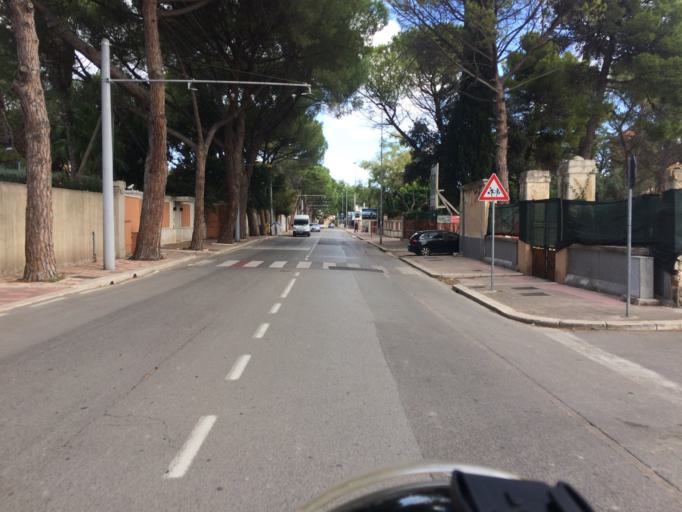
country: IT
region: Apulia
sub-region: Provincia di Bari
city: Bari
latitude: 41.0827
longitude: 16.8691
